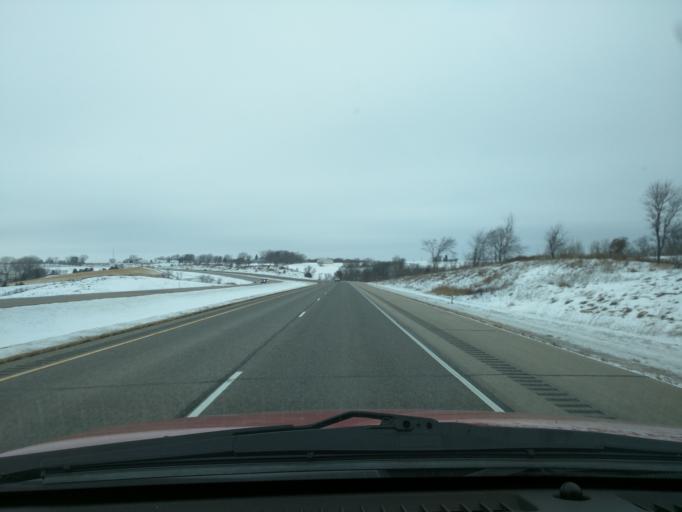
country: US
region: Minnesota
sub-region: Winona County
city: Winona
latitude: 43.9539
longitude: -91.6536
